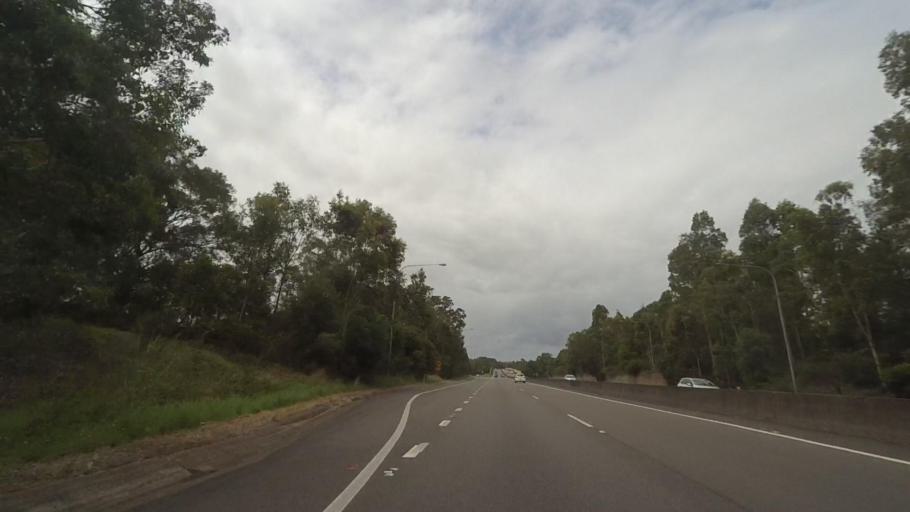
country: AU
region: New South Wales
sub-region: Port Stephens Shire
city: Raymond Terrace
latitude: -32.7604
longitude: 151.7643
